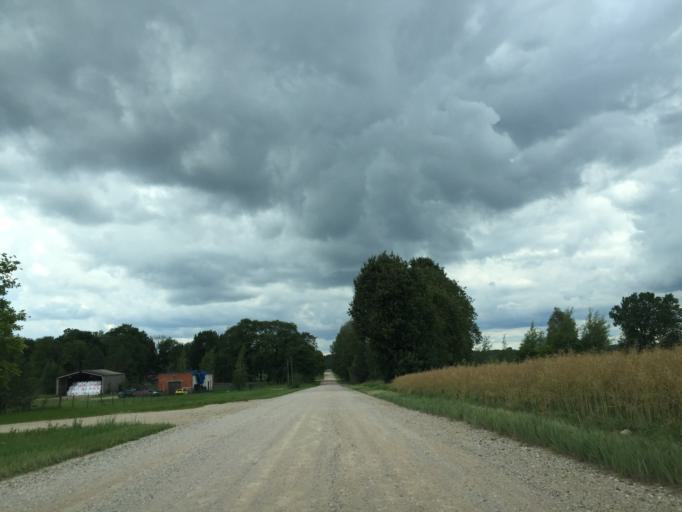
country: LV
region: Malpils
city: Malpils
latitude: 56.8582
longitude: 25.0280
